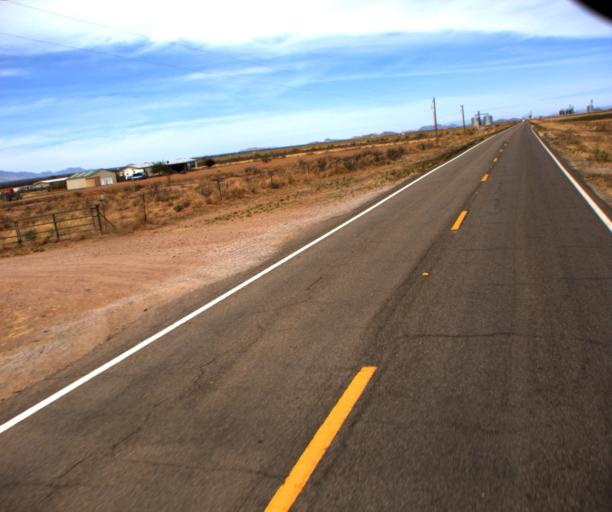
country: US
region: Arizona
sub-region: Cochise County
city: Tombstone
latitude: 31.7442
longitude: -109.6883
